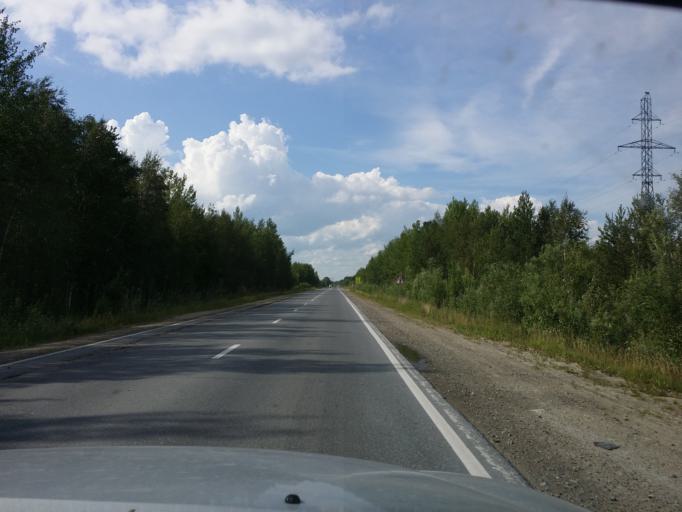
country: RU
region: Khanty-Mansiyskiy Avtonomnyy Okrug
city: Megion
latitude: 61.1455
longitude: 75.7549
